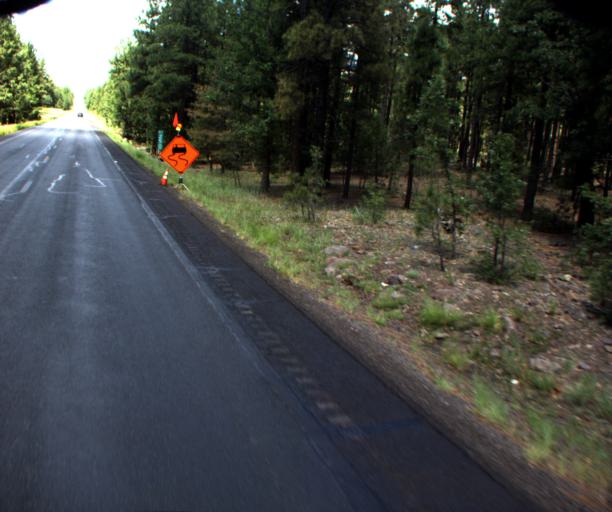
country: US
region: Arizona
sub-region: Gila County
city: Pine
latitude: 34.4779
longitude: -111.4518
